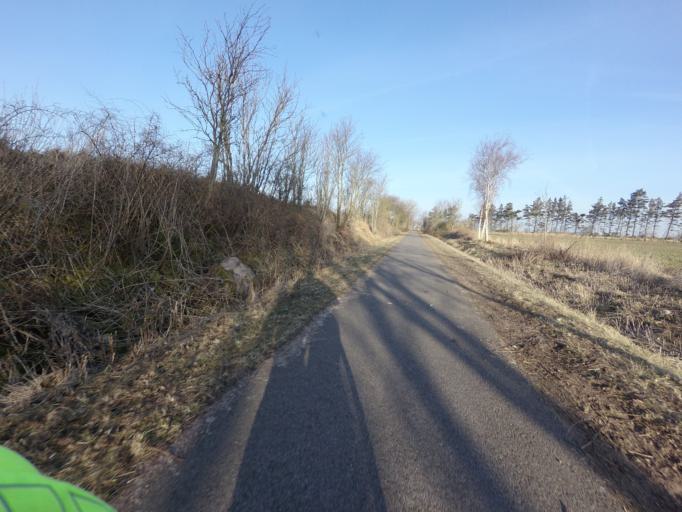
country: SE
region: Skane
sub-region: Hoganas Kommun
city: Hoganas
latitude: 56.1924
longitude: 12.6122
